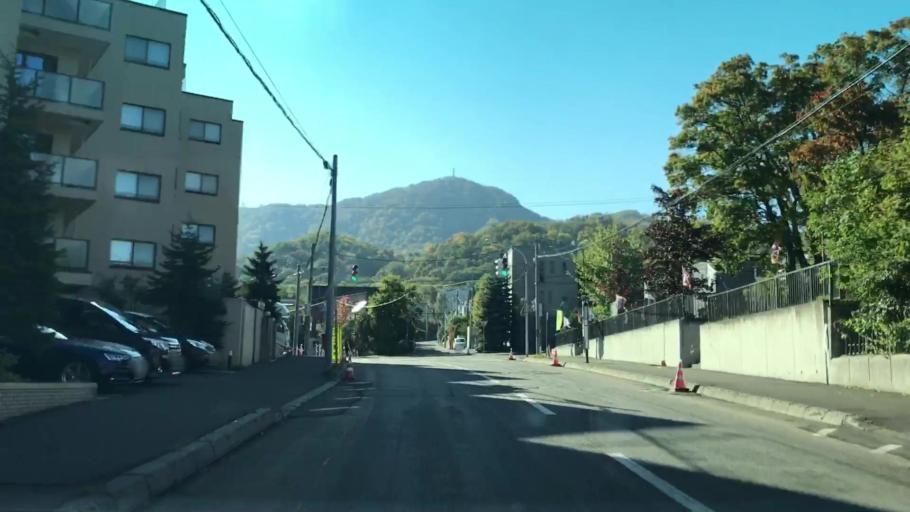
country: JP
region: Hokkaido
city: Sapporo
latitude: 43.0412
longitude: 141.3200
